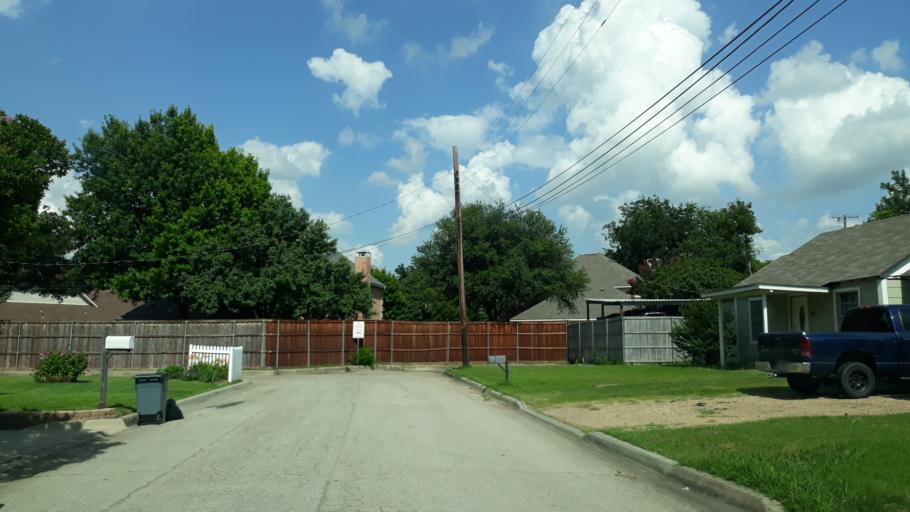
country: US
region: Texas
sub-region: Dallas County
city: Coppell
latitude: 32.9604
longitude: -97.0020
